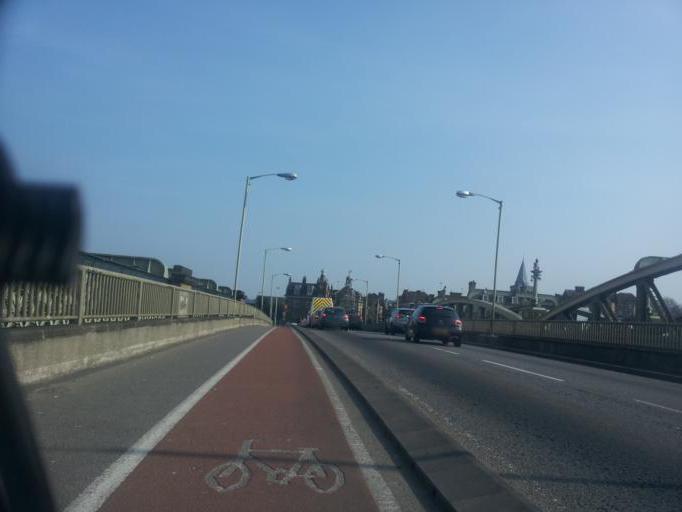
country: GB
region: England
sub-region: Medway
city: Rochester
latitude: 51.3925
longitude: 0.5009
